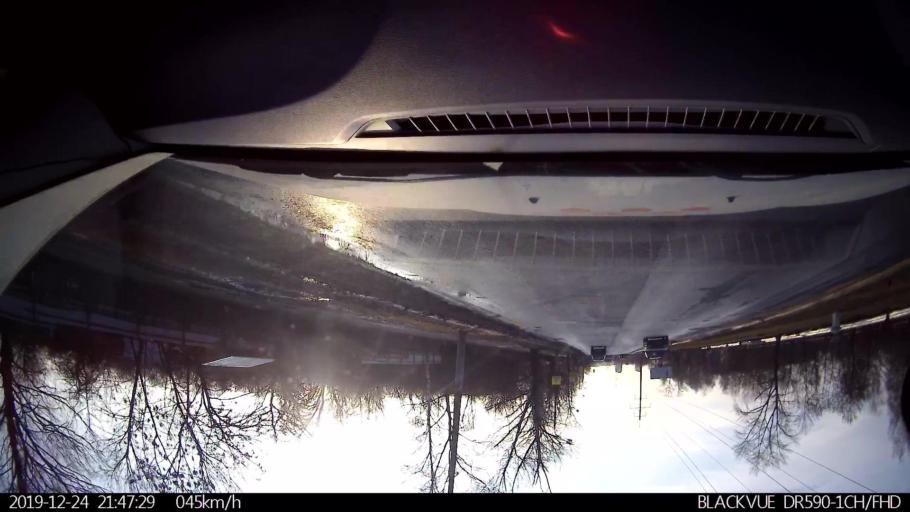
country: RU
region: Nizjnij Novgorod
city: Gorbatovka
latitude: 56.2301
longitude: 43.8407
